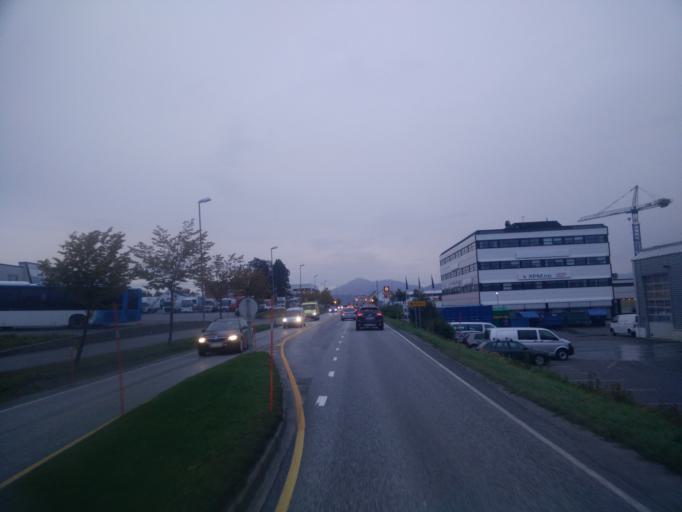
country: NO
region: More og Romsdal
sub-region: Molde
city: Molde
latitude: 62.7398
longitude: 7.1940
